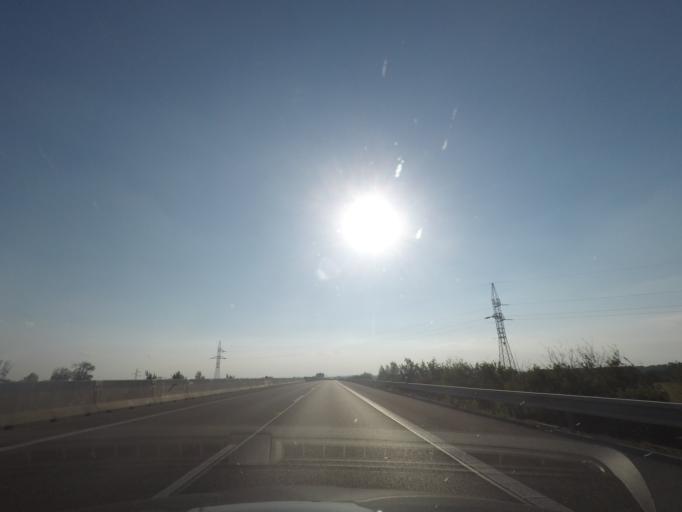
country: CZ
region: Olomoucky
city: Grygov
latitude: 49.5569
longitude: 17.2995
